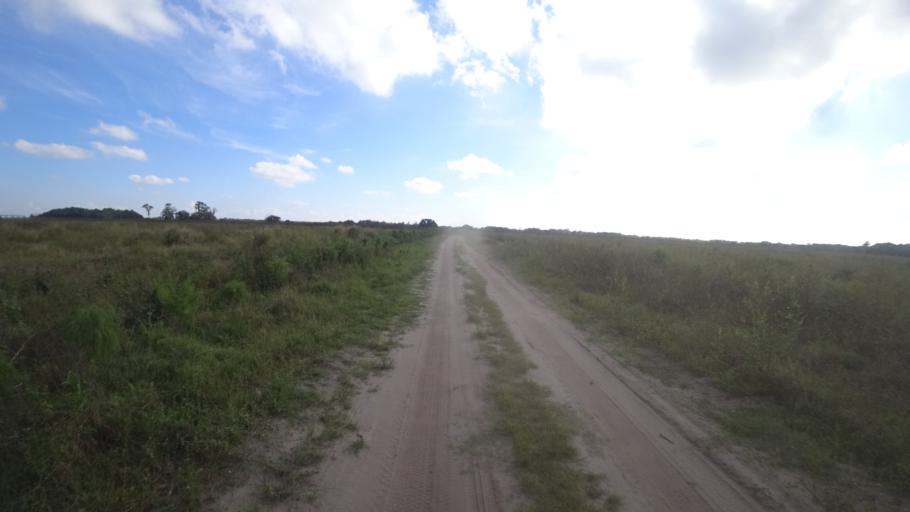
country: US
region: Florida
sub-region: DeSoto County
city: Arcadia
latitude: 27.3472
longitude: -82.1150
